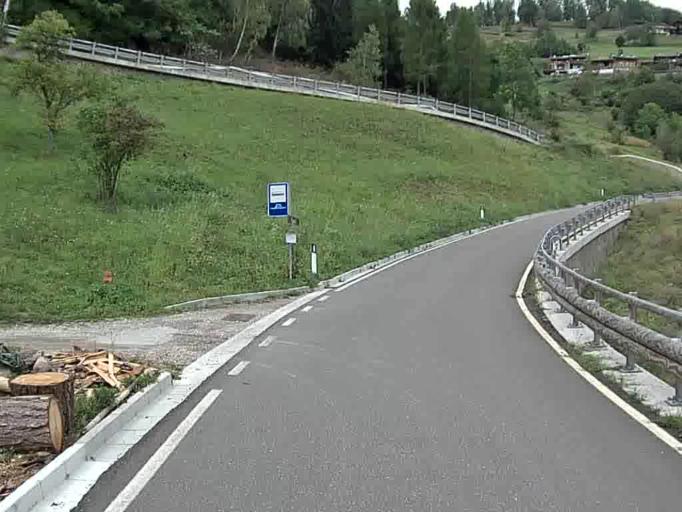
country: IT
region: Trentino-Alto Adige
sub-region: Provincia di Trento
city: Frassilongo
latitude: 46.0721
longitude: 11.3041
